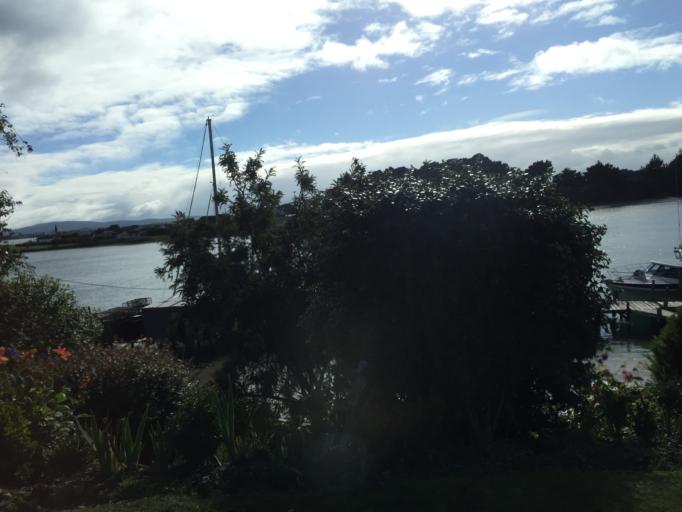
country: NZ
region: Southland
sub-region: Southland District
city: Riverton
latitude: -46.3583
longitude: 168.0149
